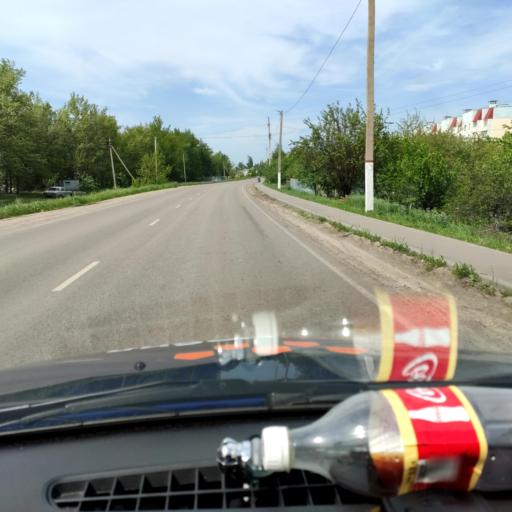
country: RU
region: Voronezj
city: Novaya Usman'
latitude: 51.6061
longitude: 39.3734
